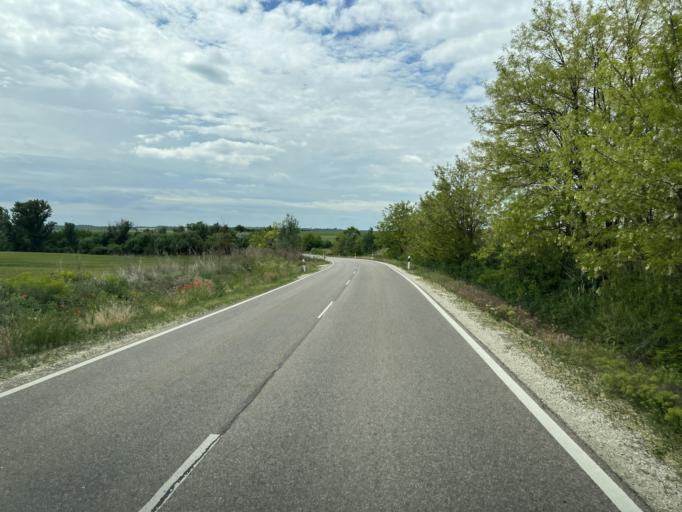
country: HU
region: Pest
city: Zsambok
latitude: 47.5251
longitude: 19.5994
